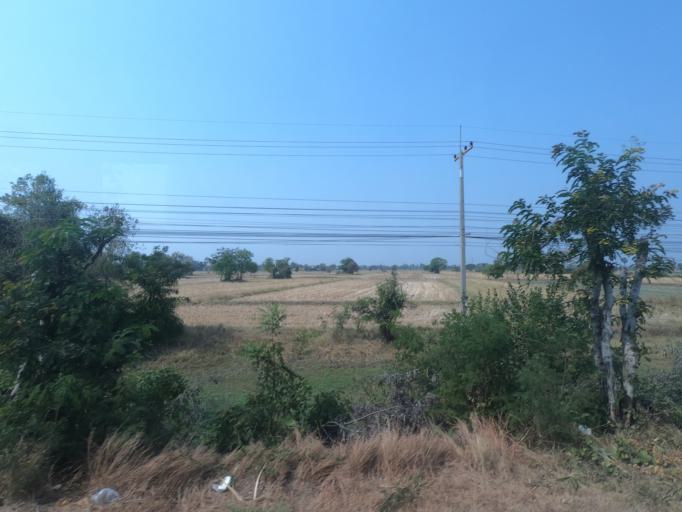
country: TH
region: Nakhon Ratchasima
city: Non Sung
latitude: 15.2278
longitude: 102.3685
